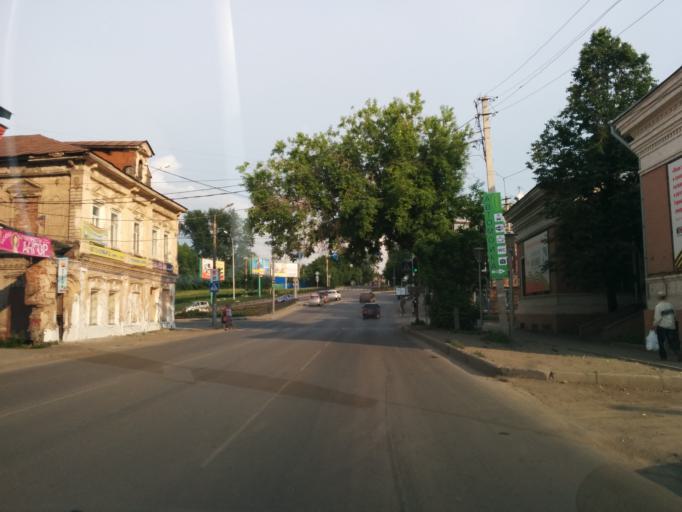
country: RU
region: Perm
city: Perm
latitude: 58.0360
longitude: 56.3101
